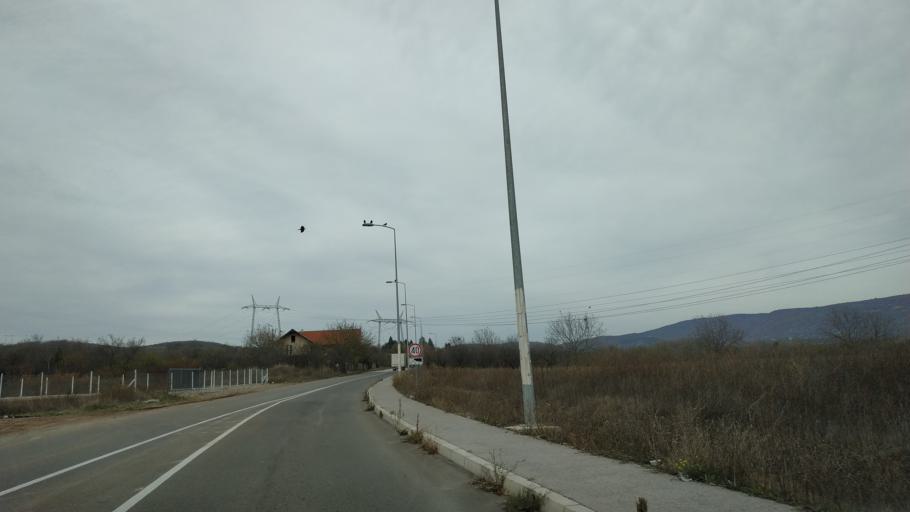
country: RS
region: Central Serbia
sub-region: Nisavski Okrug
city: Nis
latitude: 43.3435
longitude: 21.9372
